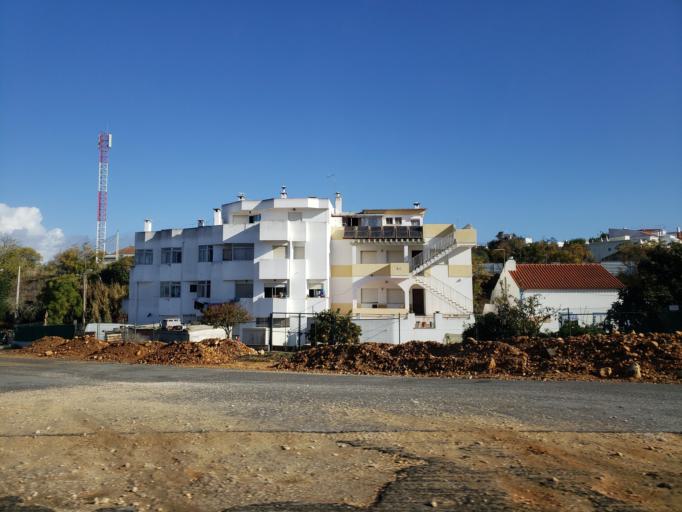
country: PT
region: Faro
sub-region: Portimao
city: Portimao
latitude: 37.1583
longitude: -8.5629
